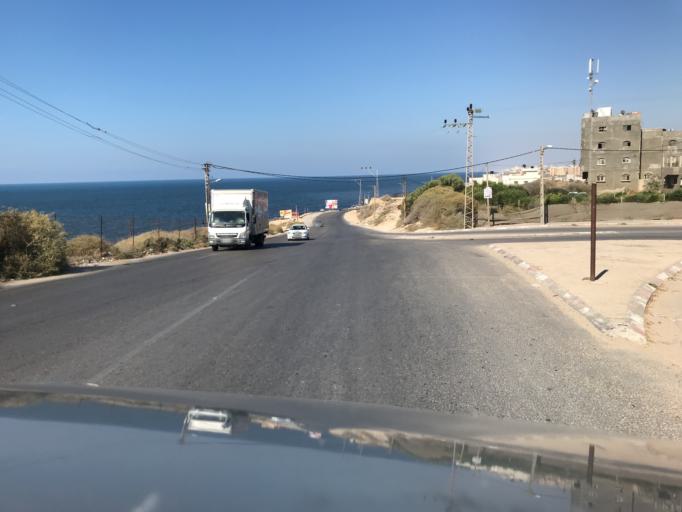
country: PS
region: Gaza Strip
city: Az Zuwaydah
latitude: 31.4566
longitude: 34.3702
